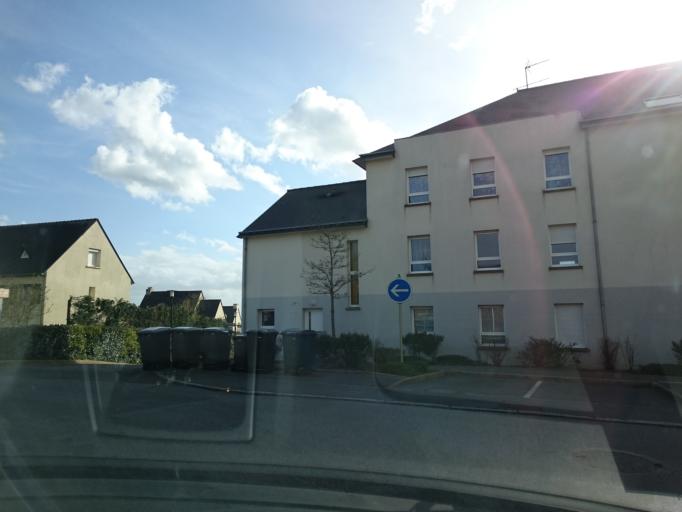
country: FR
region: Brittany
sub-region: Departement d'Ille-et-Vilaine
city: Crevin
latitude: 47.9363
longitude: -1.6608
